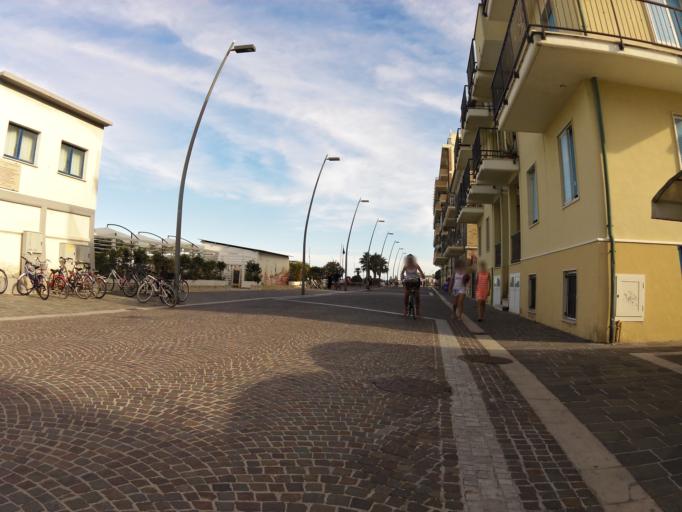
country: IT
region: The Marches
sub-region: Provincia di Macerata
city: Porto Recanati
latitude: 43.4289
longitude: 13.6676
